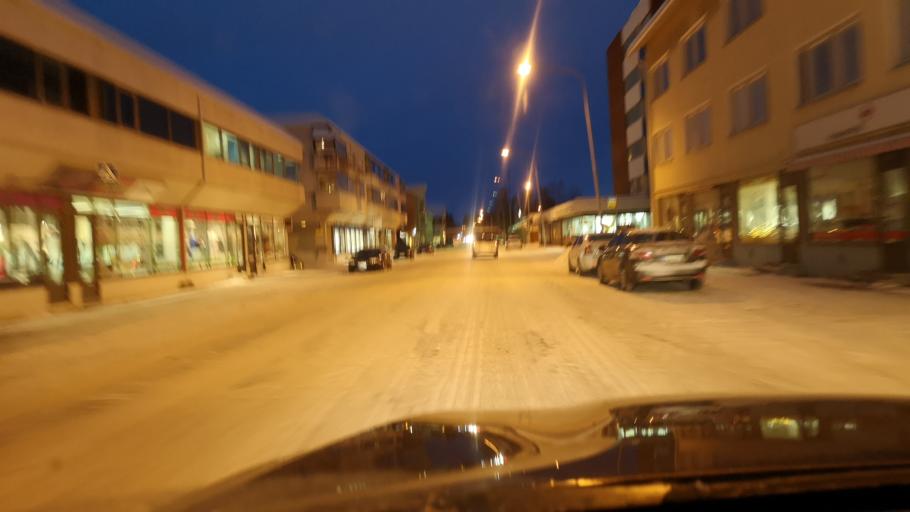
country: FI
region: Varsinais-Suomi
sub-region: Loimaa
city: Loimaa
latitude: 60.8510
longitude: 23.0600
